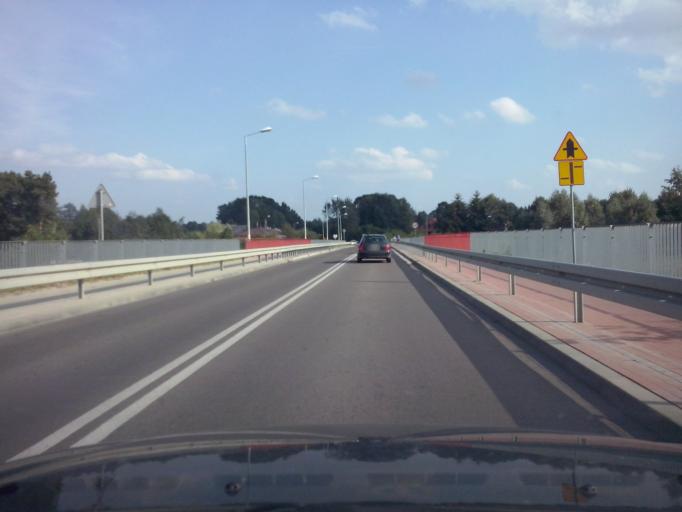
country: PL
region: Subcarpathian Voivodeship
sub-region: Powiat kolbuszowski
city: Cmolas
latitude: 50.2609
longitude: 21.7254
